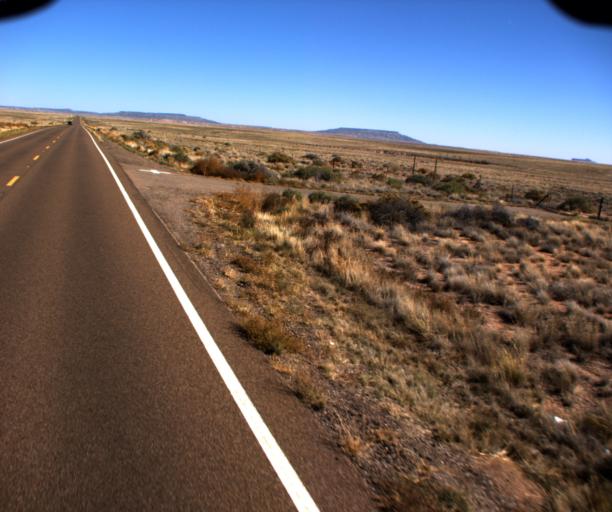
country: US
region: Arizona
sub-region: Navajo County
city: Joseph City
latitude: 35.1432
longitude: -110.4806
